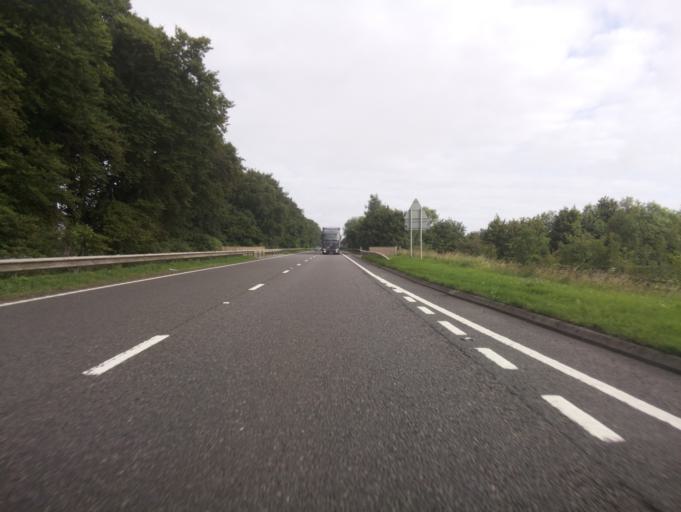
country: GB
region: England
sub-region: Gloucestershire
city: Coates
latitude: 51.7726
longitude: -2.0250
